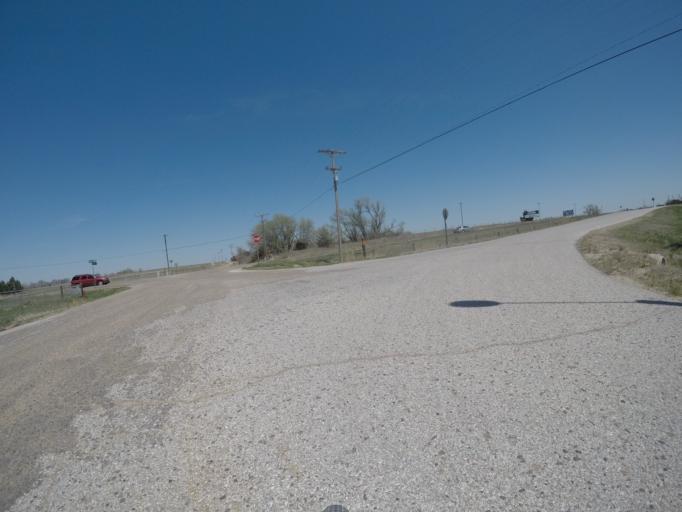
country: US
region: Kansas
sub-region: Pratt County
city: Pratt
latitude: 37.6415
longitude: -98.7668
